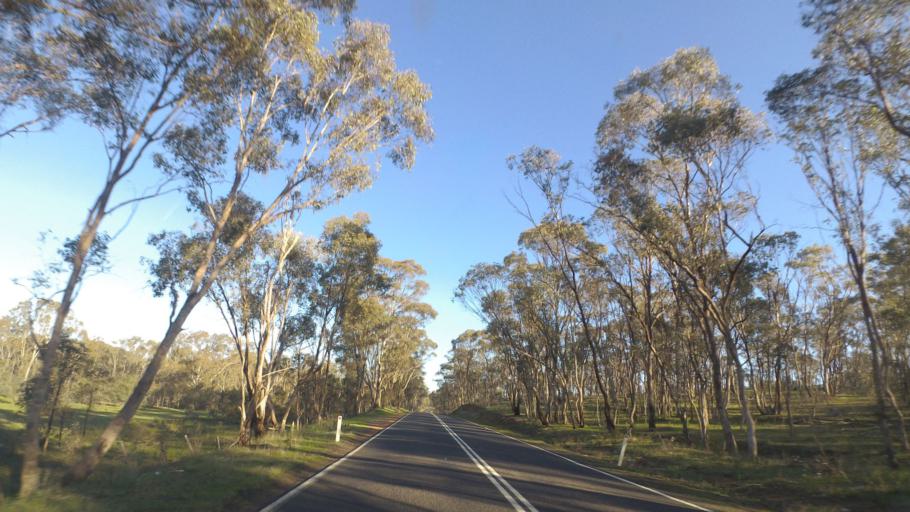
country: AU
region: Victoria
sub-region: Greater Bendigo
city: Kennington
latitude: -36.9012
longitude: 144.4954
